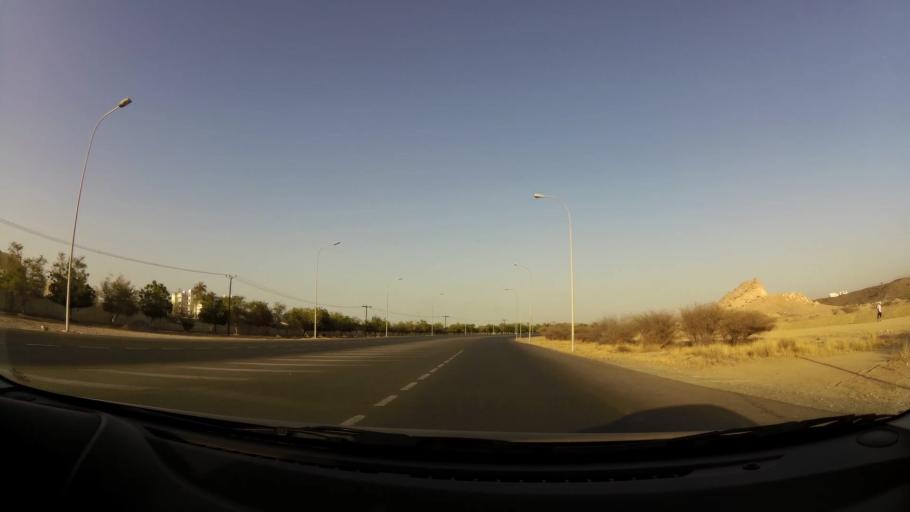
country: OM
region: Muhafazat Masqat
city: As Sib al Jadidah
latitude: 23.5819
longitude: 58.1709
